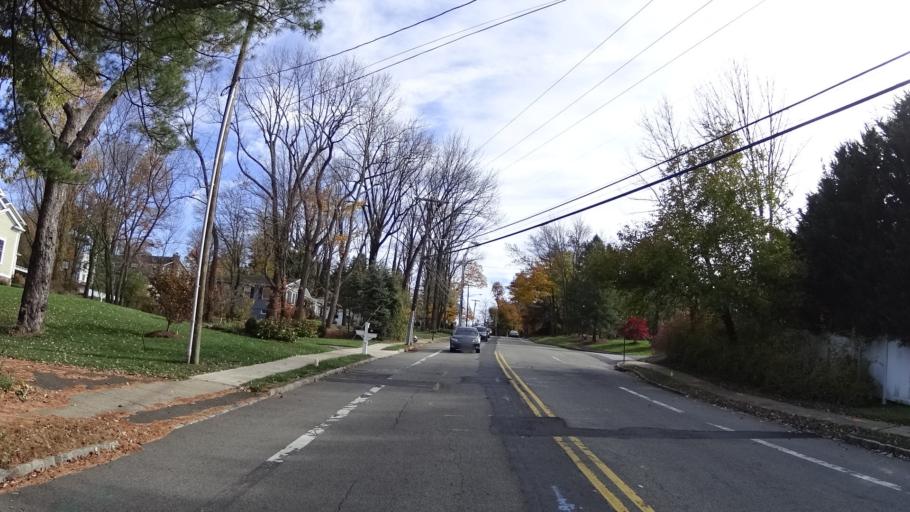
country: US
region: New Jersey
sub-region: Union County
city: New Providence
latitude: 40.7240
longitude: -74.4065
